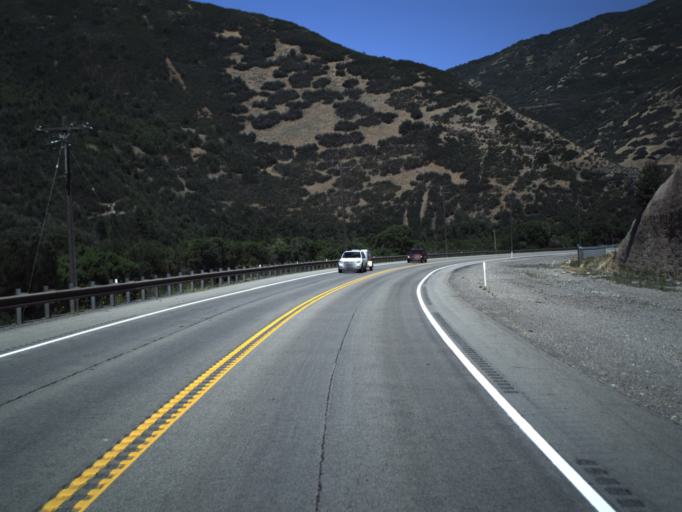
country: US
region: Utah
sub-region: Utah County
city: Mapleton
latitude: 40.0449
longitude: -111.5475
